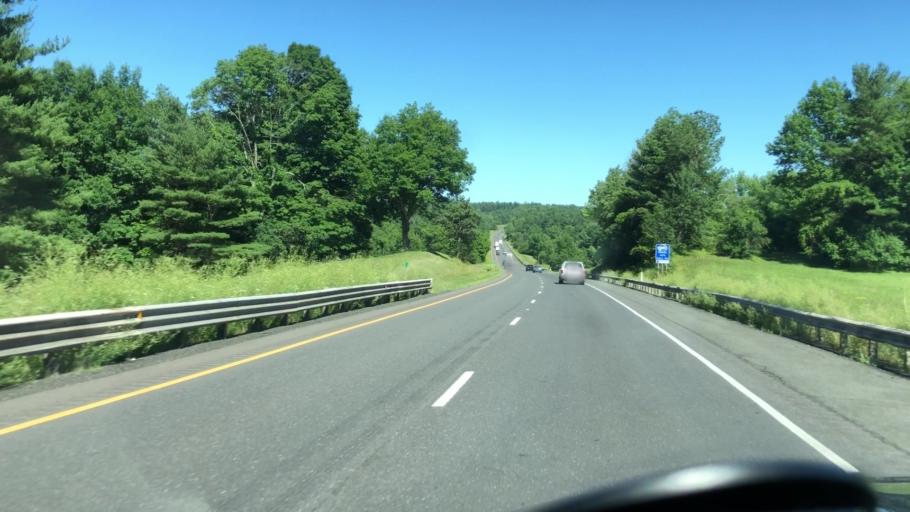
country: US
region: Massachusetts
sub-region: Berkshire County
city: Stockbridge
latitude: 42.3046
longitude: -73.3412
